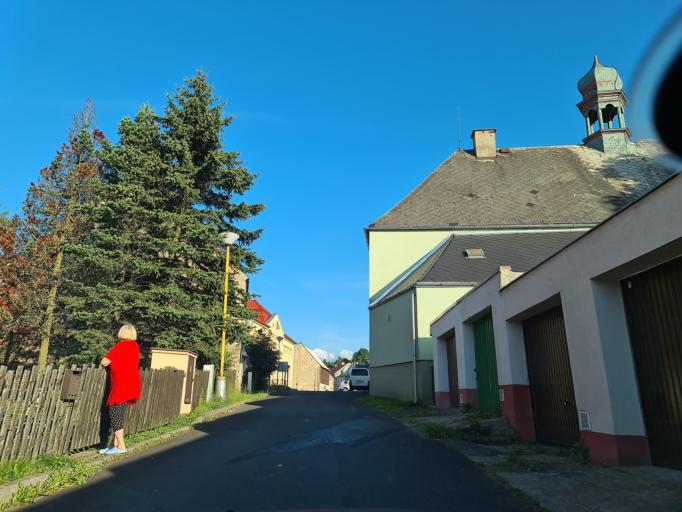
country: DE
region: Saxony
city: Deutschneudorf
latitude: 50.6067
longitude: 13.4356
